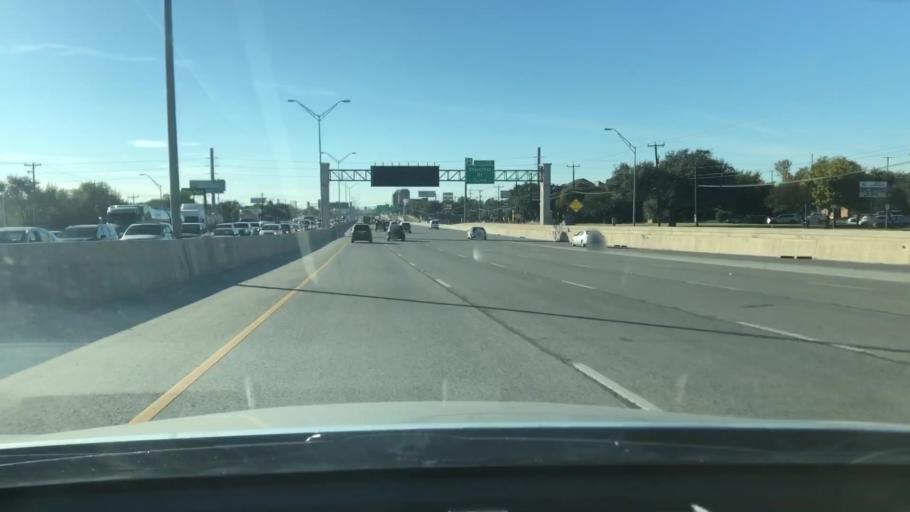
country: US
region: Texas
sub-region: Bexar County
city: Windcrest
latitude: 29.5164
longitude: -98.4124
